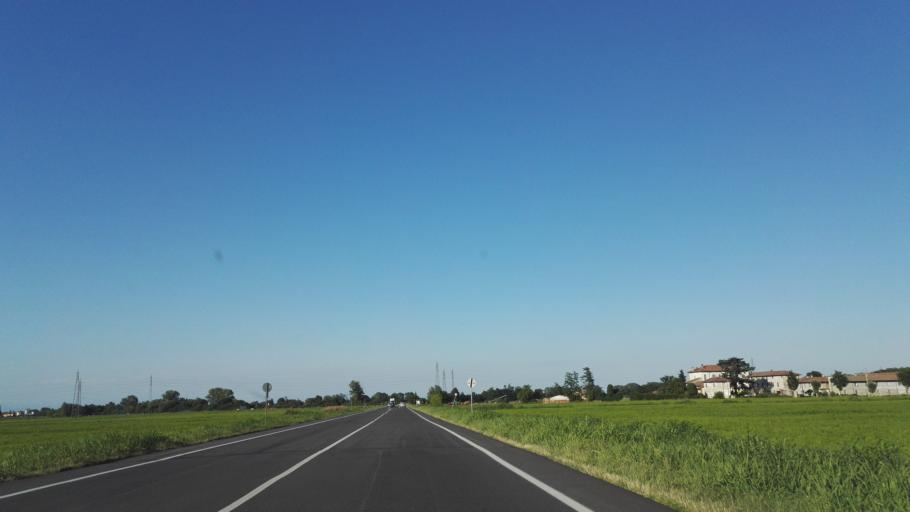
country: IT
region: Lombardy
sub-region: Citta metropolitana di Milano
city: Locate di Triulzi
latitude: 45.3688
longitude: 9.2513
